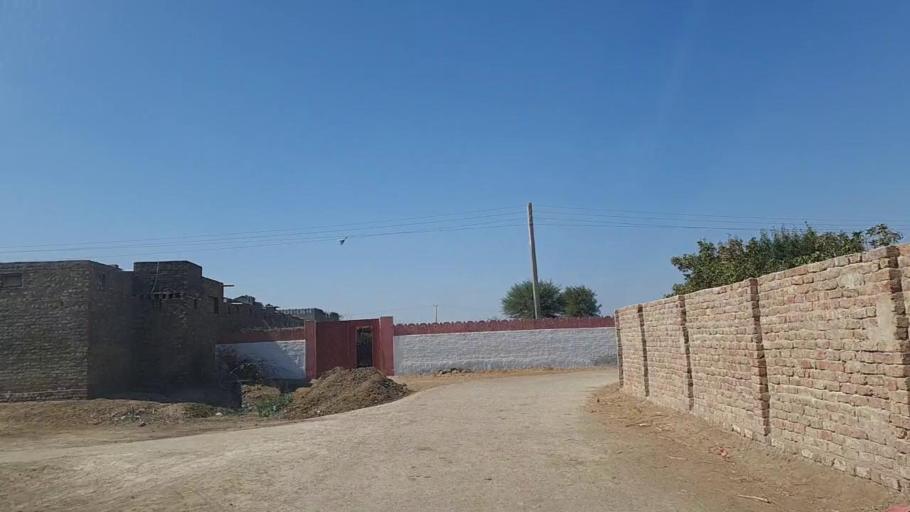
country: PK
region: Sindh
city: Samaro
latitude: 25.1037
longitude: 69.3877
